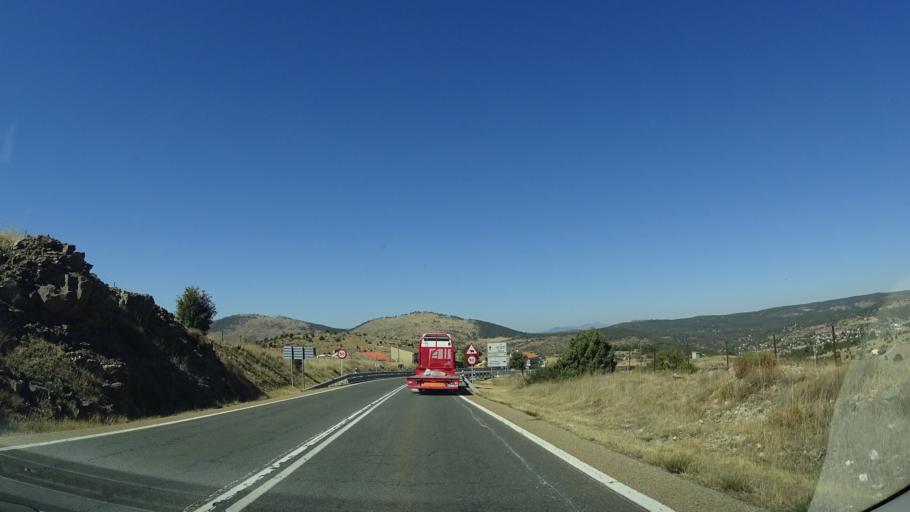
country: ES
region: Madrid
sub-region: Provincia de Madrid
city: Santa Maria de la Alameda
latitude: 40.5607
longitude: -4.2409
